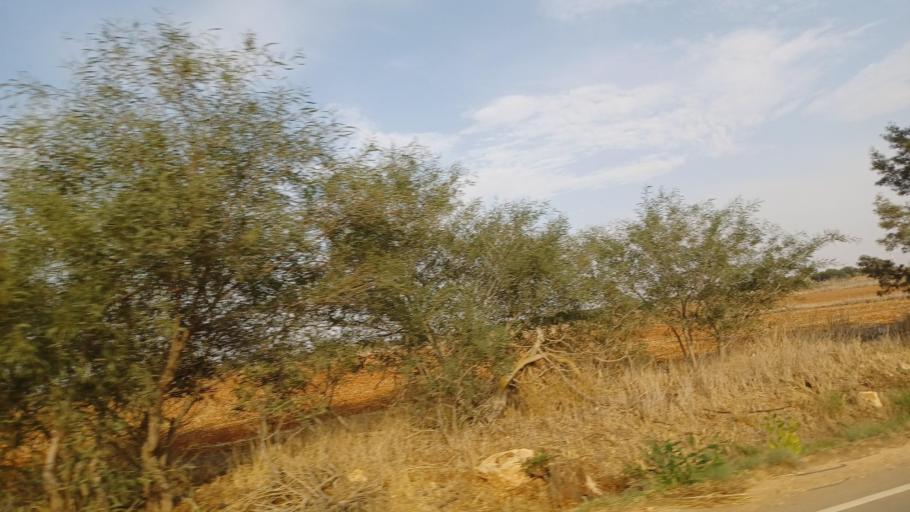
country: CY
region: Ammochostos
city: Frenaros
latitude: 35.0635
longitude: 33.8887
